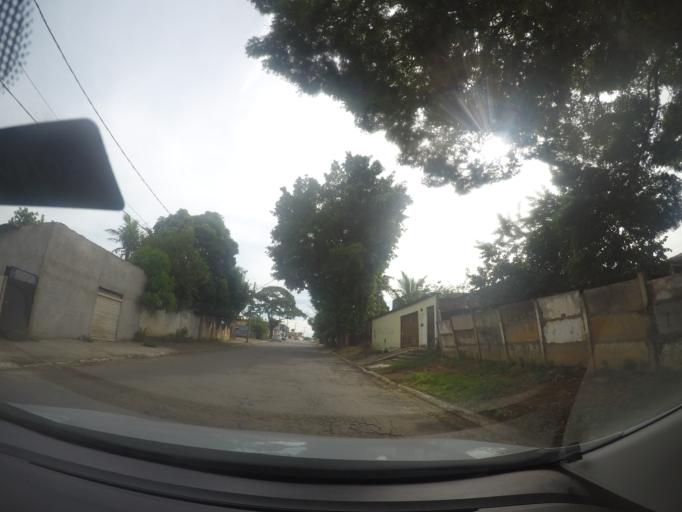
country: BR
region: Goias
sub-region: Goiania
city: Goiania
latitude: -16.6578
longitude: -49.3054
